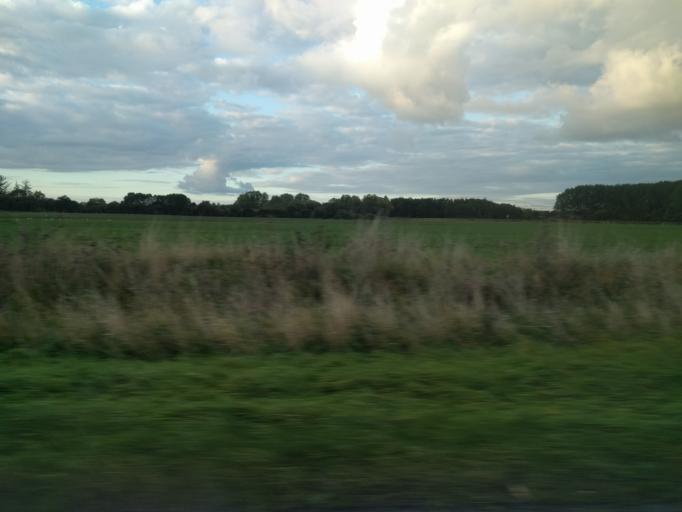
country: DK
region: Zealand
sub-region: Slagelse Kommune
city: Forlev
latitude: 55.3698
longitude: 11.2483
